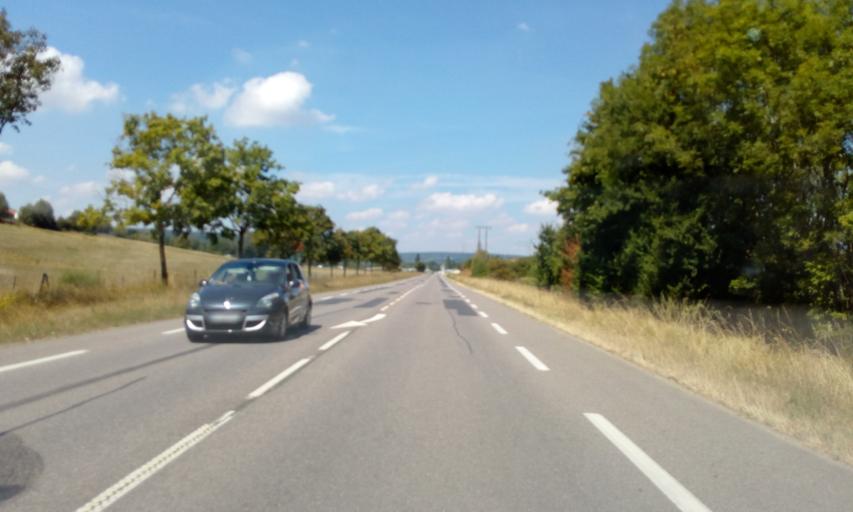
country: FR
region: Lorraine
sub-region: Departement de Meurthe-et-Moselle
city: Dieulouard
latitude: 48.8638
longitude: 6.0727
